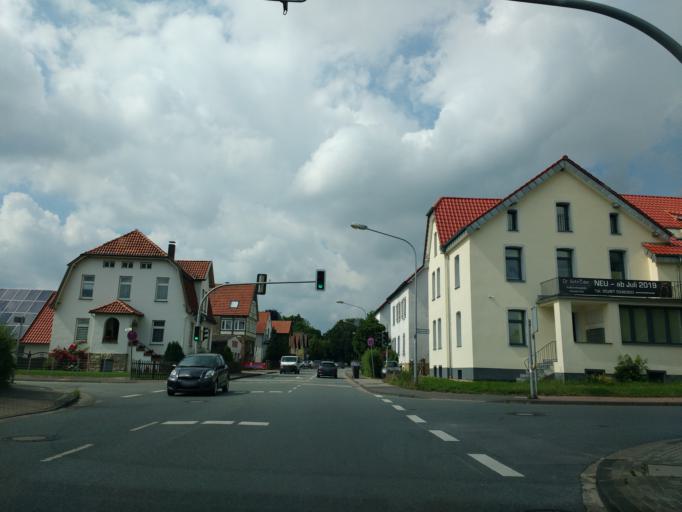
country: DE
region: North Rhine-Westphalia
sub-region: Regierungsbezirk Detmold
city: Lemgo
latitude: 52.0317
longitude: 8.9056
